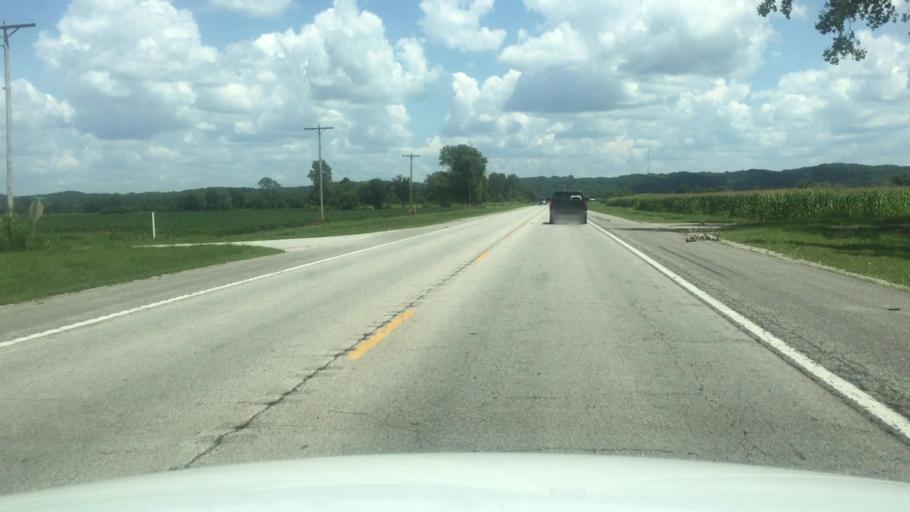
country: US
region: Kansas
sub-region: Atchison County
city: Atchison
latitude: 39.5569
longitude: -95.0791
